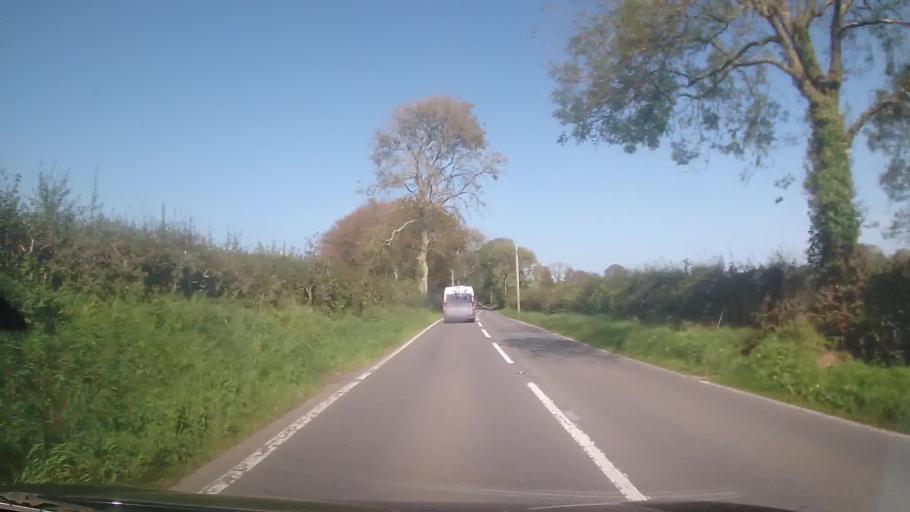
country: GB
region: Wales
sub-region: Pembrokeshire
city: Crymych
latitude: 52.0186
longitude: -4.7006
